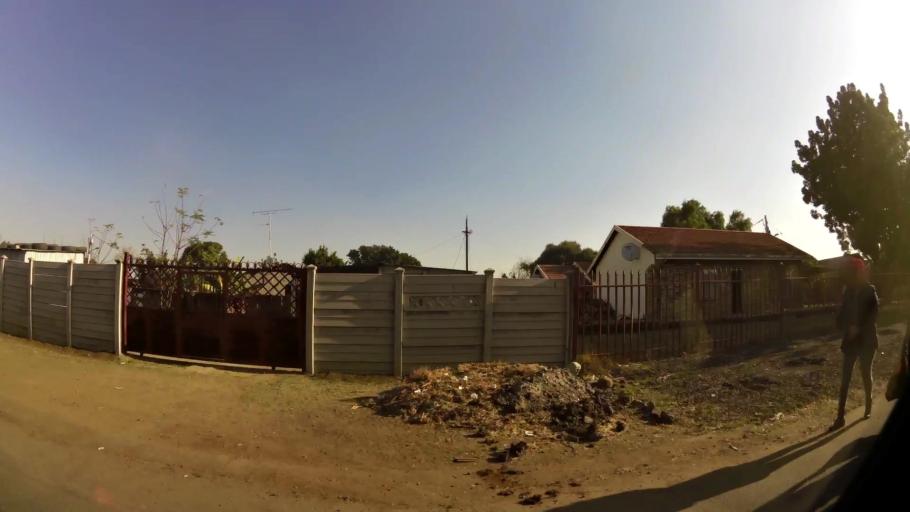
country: ZA
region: North-West
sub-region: Bojanala Platinum District Municipality
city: Rustenburg
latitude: -25.6415
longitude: 27.2387
